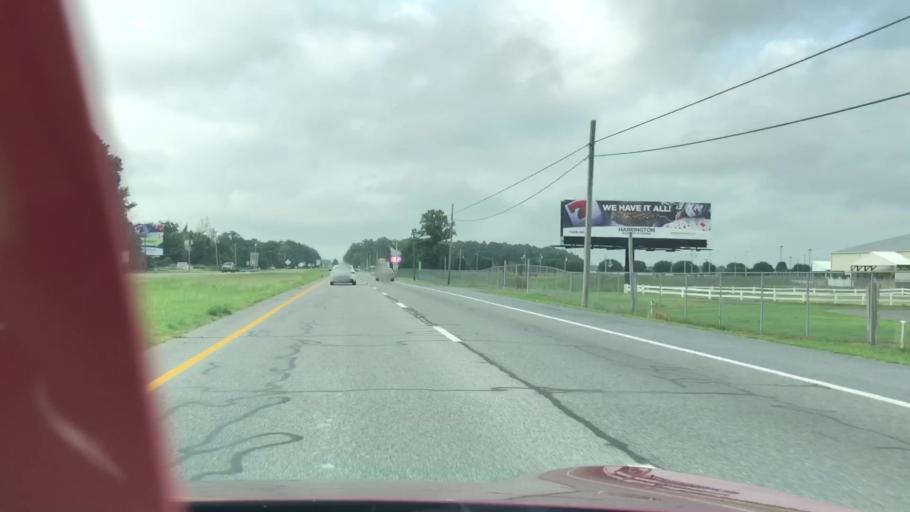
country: US
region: Delaware
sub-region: Kent County
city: Harrington
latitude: 38.9114
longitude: -75.5697
